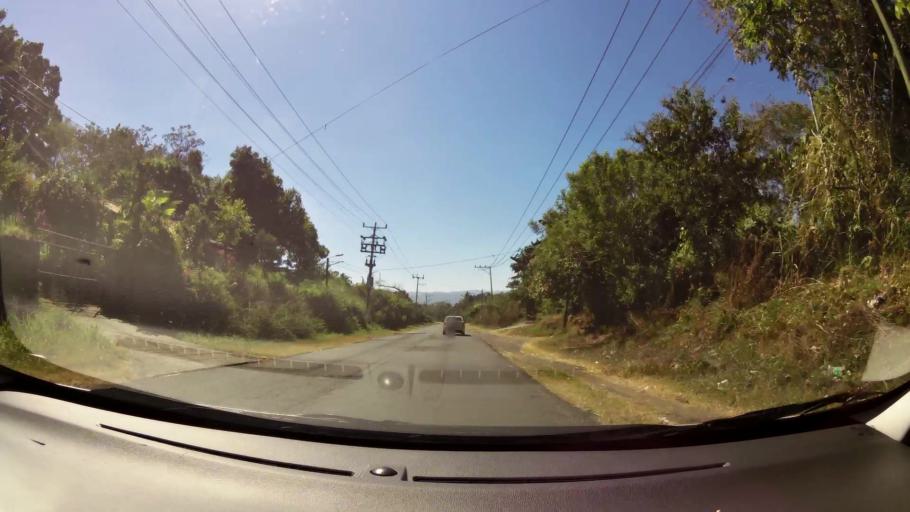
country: SV
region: La Libertad
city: San Juan Opico
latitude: 13.8181
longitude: -89.3563
